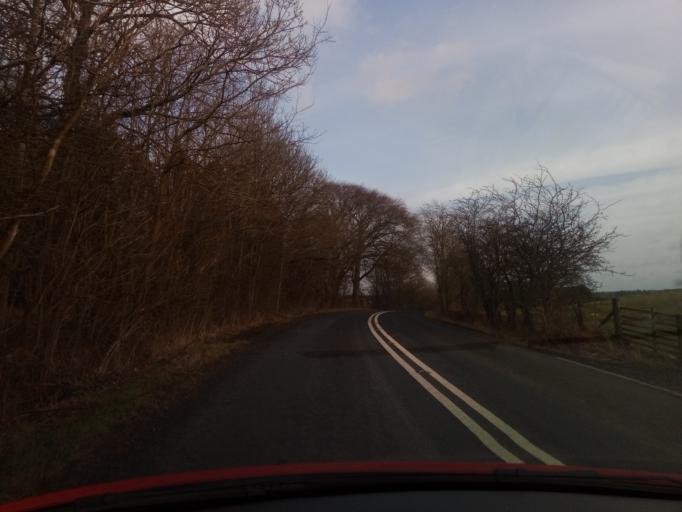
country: GB
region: England
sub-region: Northumberland
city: Acomb
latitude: 55.0996
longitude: -2.0449
